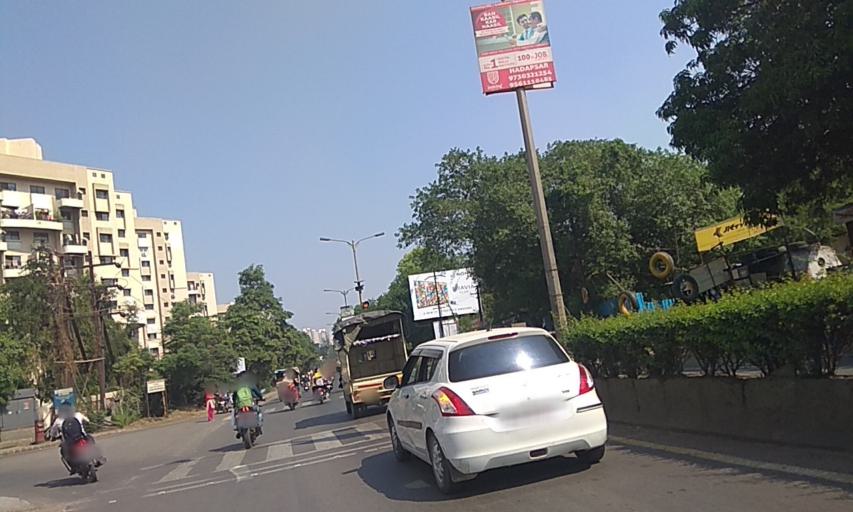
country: IN
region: Maharashtra
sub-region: Pune Division
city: Pune
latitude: 18.5082
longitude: 73.9295
